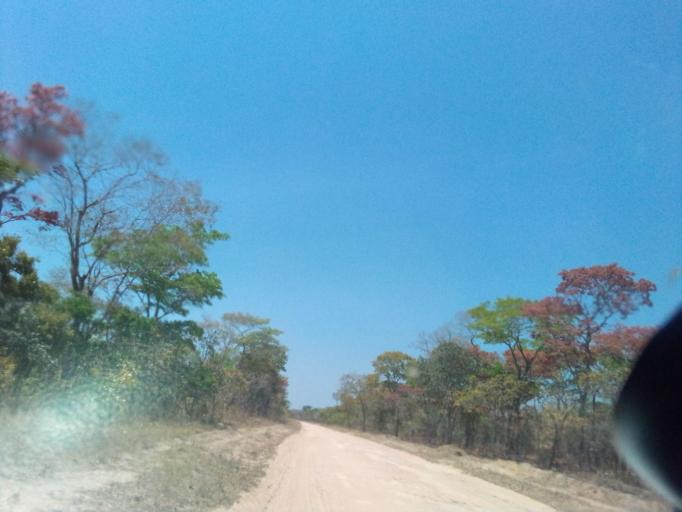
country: ZM
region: Northern
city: Mpika
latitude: -12.2390
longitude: 30.6610
